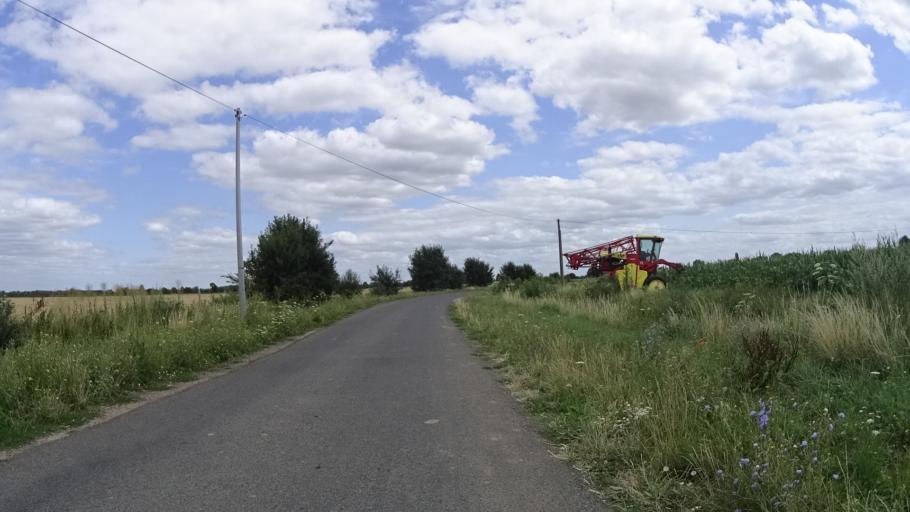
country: FR
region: Pays de la Loire
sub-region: Departement de Maine-et-Loire
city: La Menitre
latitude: 47.4036
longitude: -0.2407
